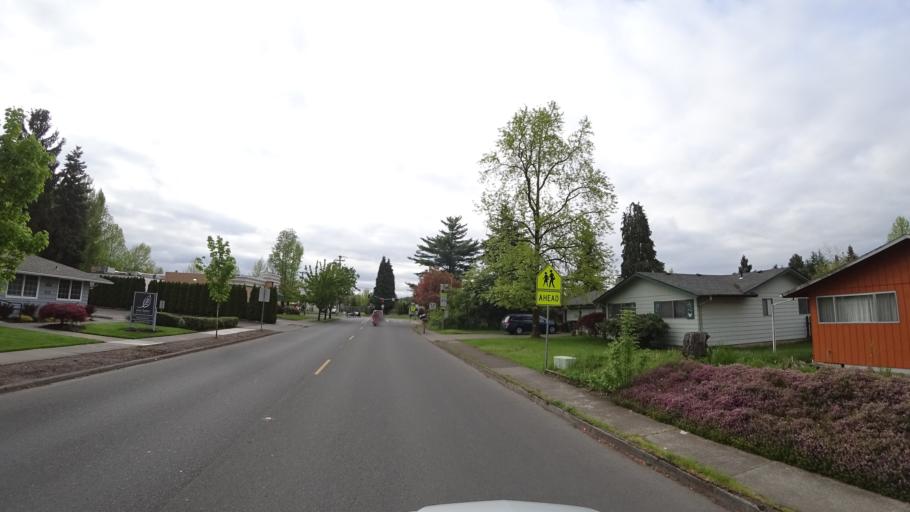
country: US
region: Oregon
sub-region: Washington County
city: Hillsboro
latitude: 45.5311
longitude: -122.9670
